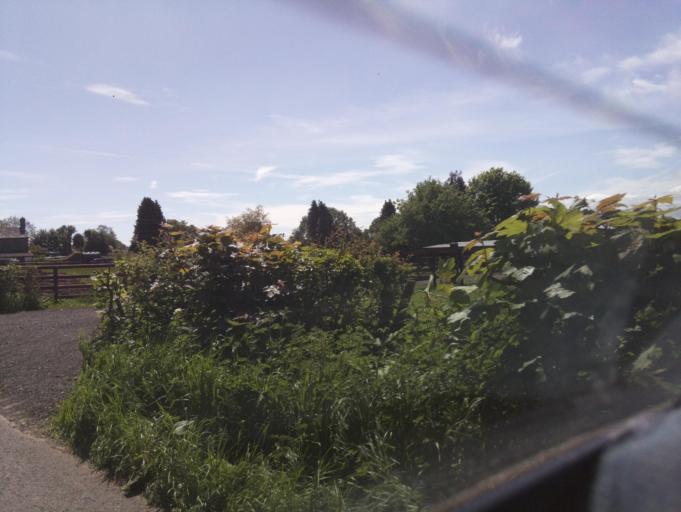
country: GB
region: Wales
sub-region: Monmouthshire
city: Llangwm
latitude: 51.7175
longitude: -2.7633
